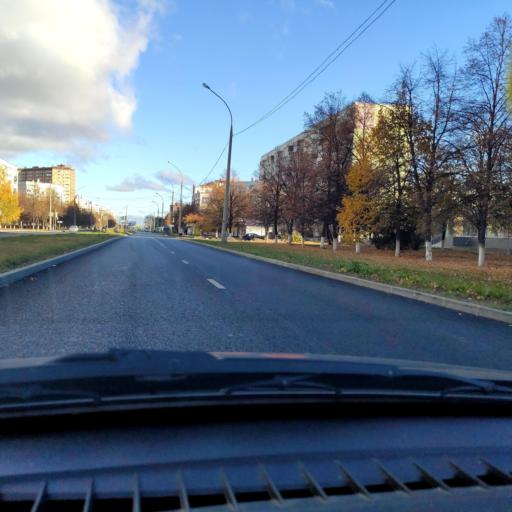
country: RU
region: Samara
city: Tol'yatti
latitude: 53.5372
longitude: 49.3296
